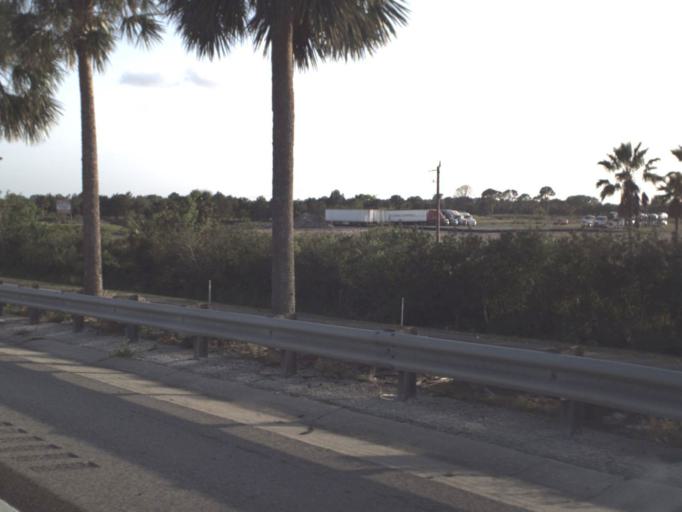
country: US
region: Florida
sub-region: Brevard County
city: Titusville
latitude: 28.5497
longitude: -80.8518
